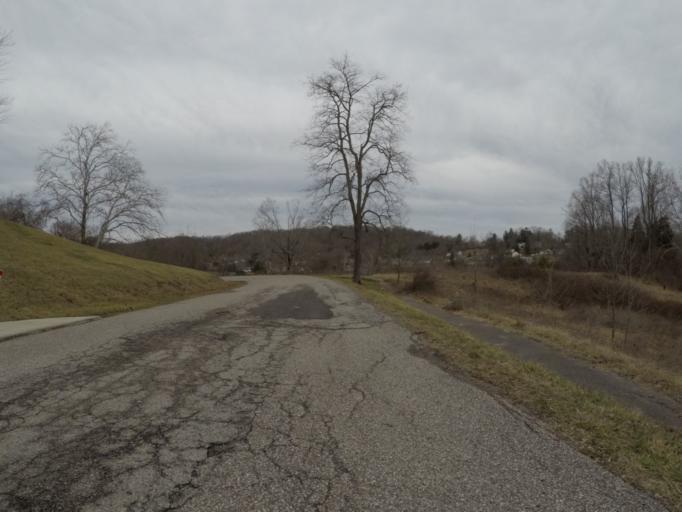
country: US
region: Ohio
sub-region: Lawrence County
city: Burlington
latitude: 38.3814
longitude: -82.5128
